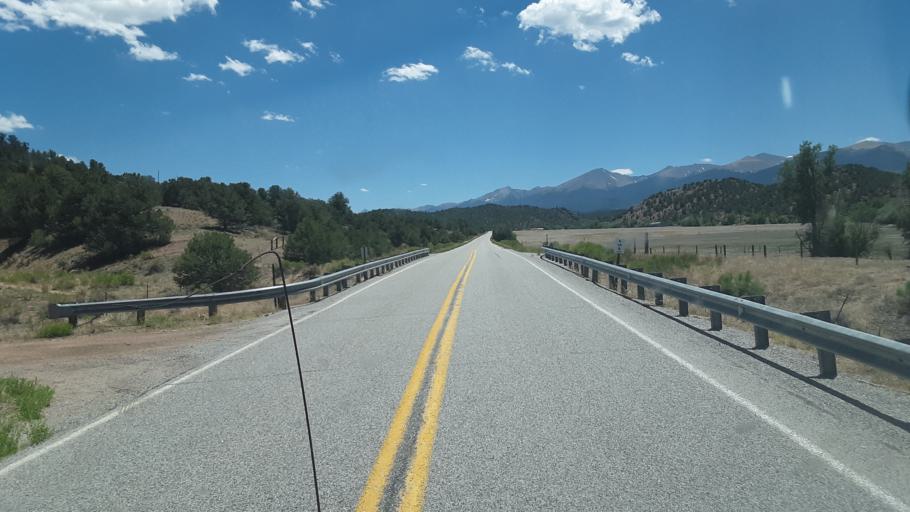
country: US
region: Colorado
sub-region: Custer County
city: Westcliffe
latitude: 38.3490
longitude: -105.5943
